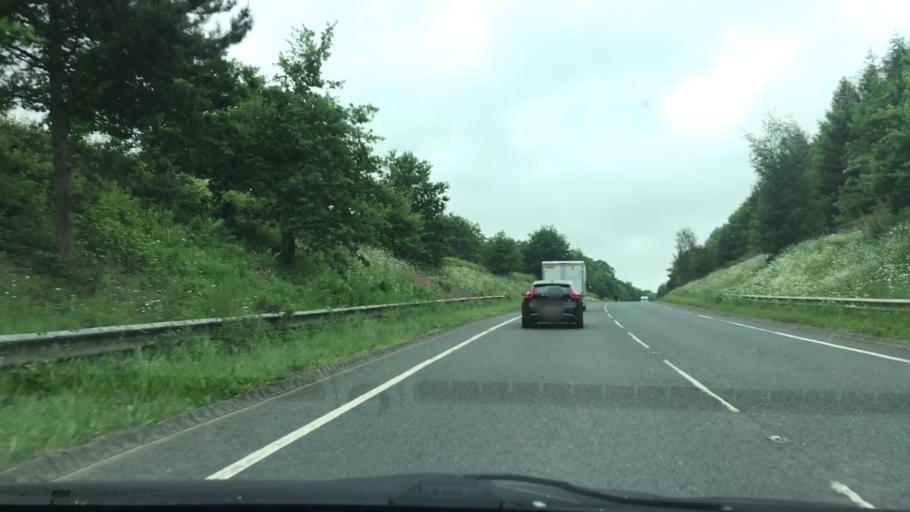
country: GB
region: England
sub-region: North Yorkshire
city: Knaresborough
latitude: 53.9698
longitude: -1.4846
